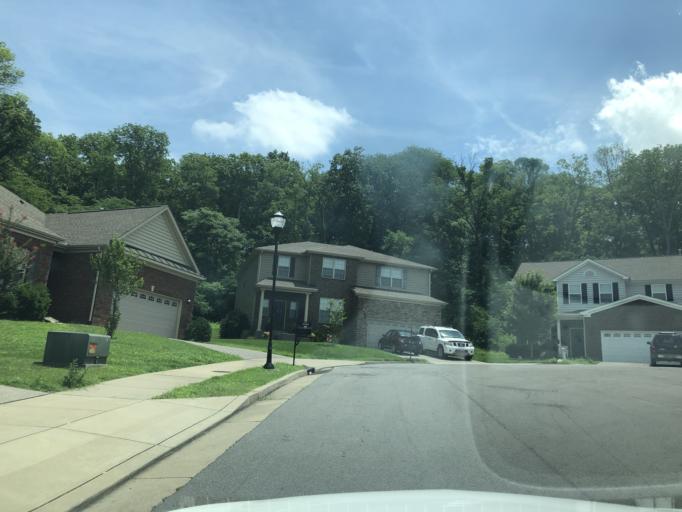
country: US
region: Tennessee
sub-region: Rutherford County
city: La Vergne
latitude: 36.0252
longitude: -86.6382
